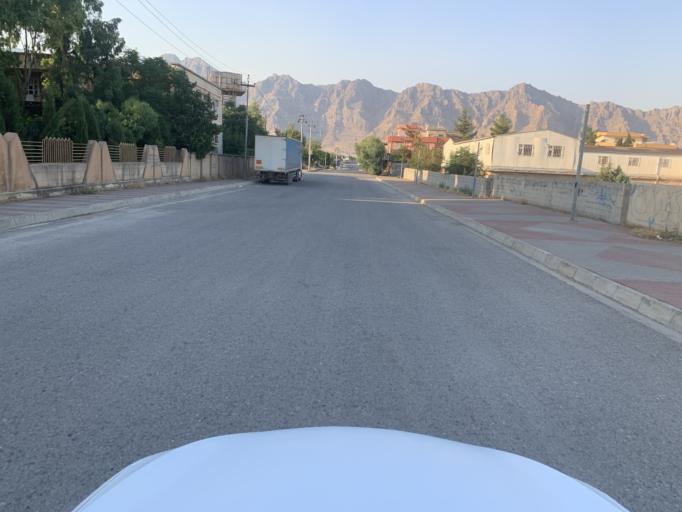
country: IQ
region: As Sulaymaniyah
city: Raniye
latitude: 36.2420
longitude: 44.8789
